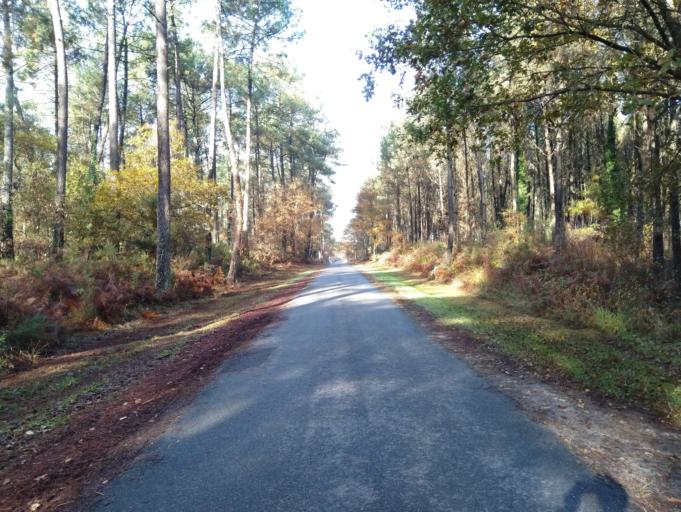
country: FR
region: Aquitaine
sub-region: Departement des Landes
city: Mees
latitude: 43.7050
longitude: -1.1270
